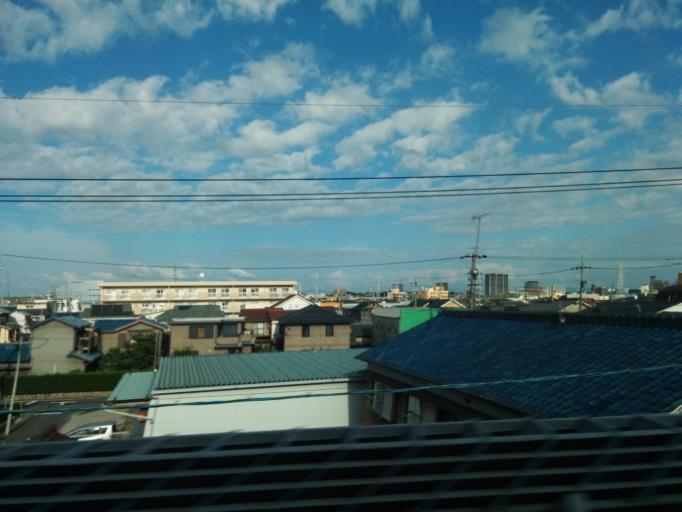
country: JP
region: Aichi
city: Obu
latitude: 35.0790
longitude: 136.9353
